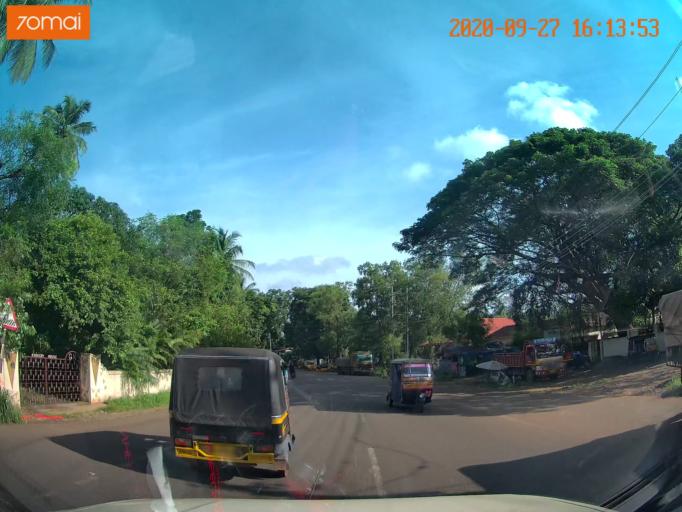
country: IN
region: Kerala
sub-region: Thrissur District
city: Trichur
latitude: 10.4670
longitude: 76.2455
